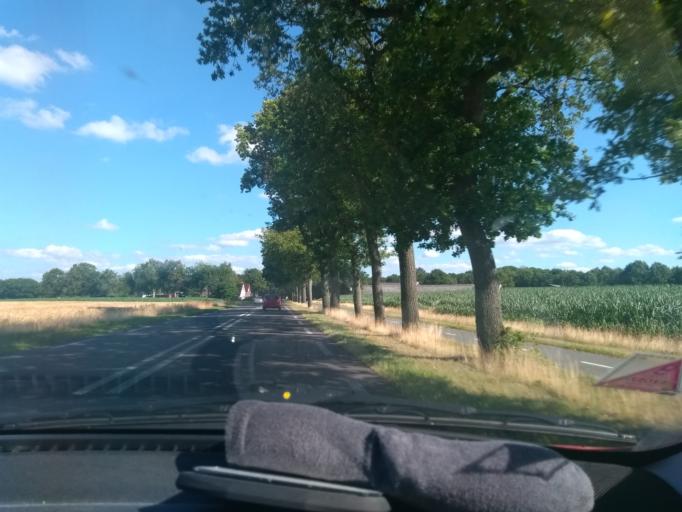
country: NL
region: Drenthe
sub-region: Gemeente Tynaarlo
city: Vries
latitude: 53.0852
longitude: 6.5653
